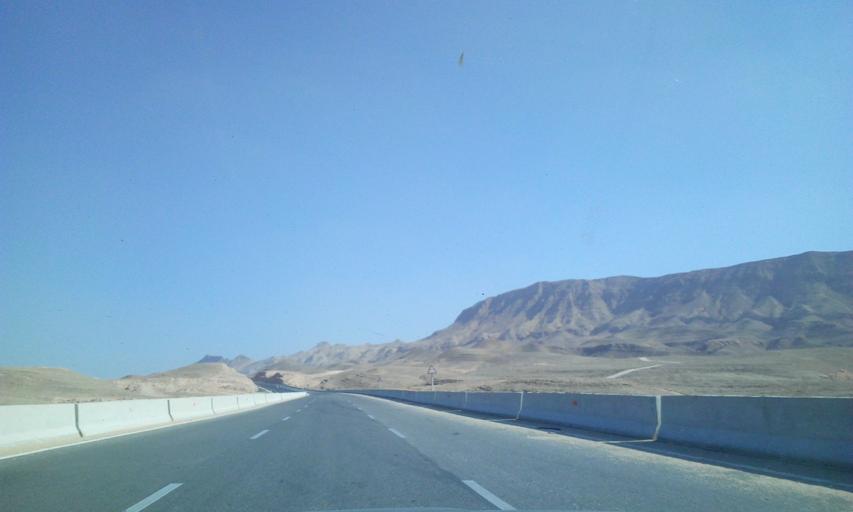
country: EG
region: As Suways
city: Ain Sukhna
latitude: 29.4646
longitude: 32.3262
